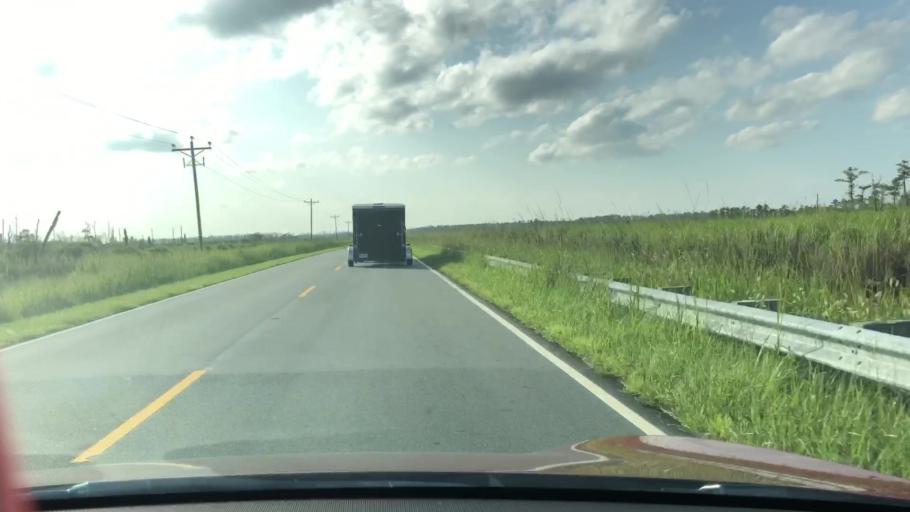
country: US
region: North Carolina
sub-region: Dare County
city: Wanchese
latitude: 35.6276
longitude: -75.8491
